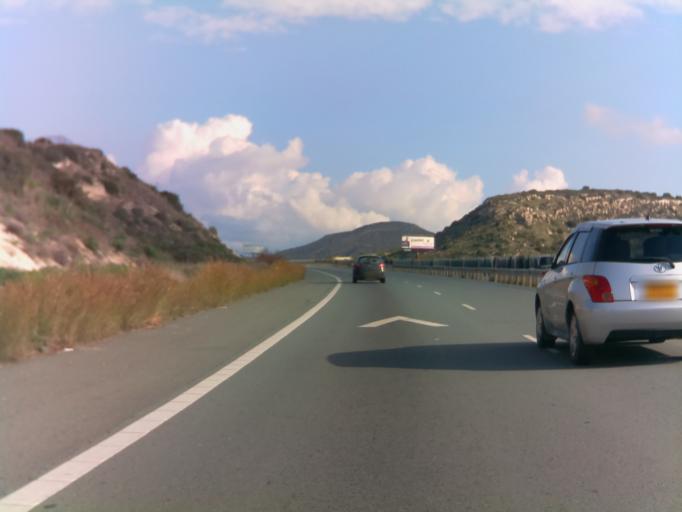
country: CY
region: Larnaka
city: Kofinou
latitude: 34.7686
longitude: 33.3344
